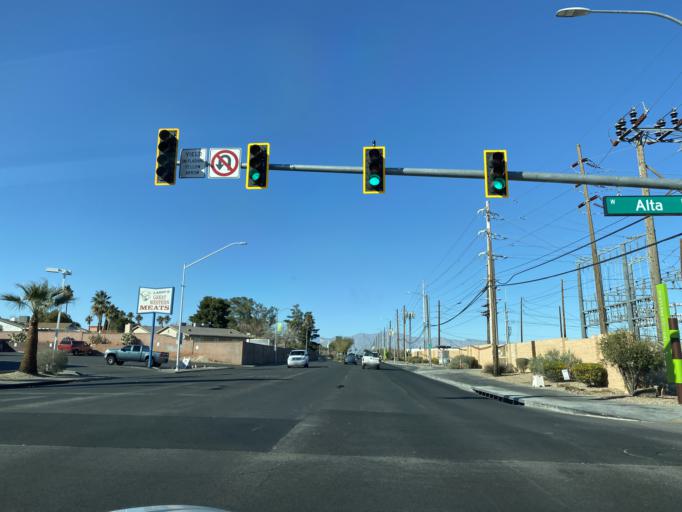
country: US
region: Nevada
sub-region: Clark County
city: Las Vegas
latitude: 36.1661
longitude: -115.1925
